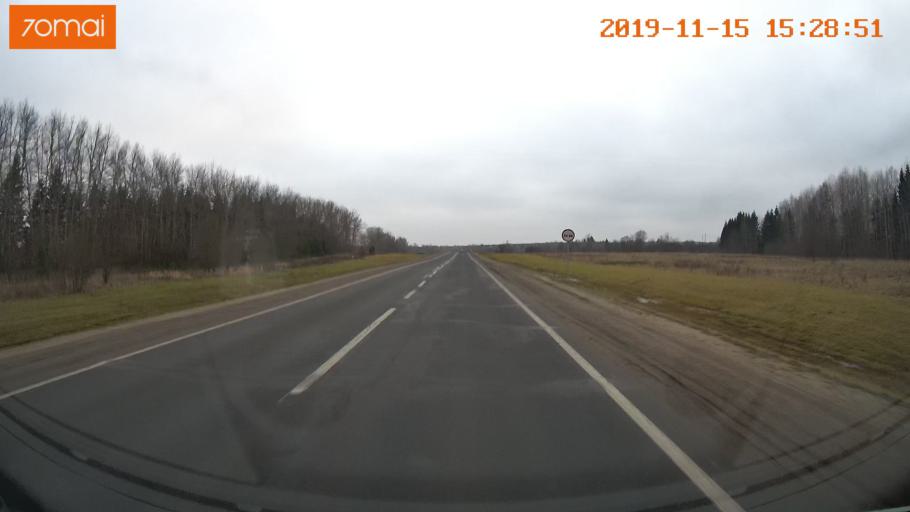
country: RU
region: Jaroslavl
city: Danilov
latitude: 58.1275
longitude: 40.1287
